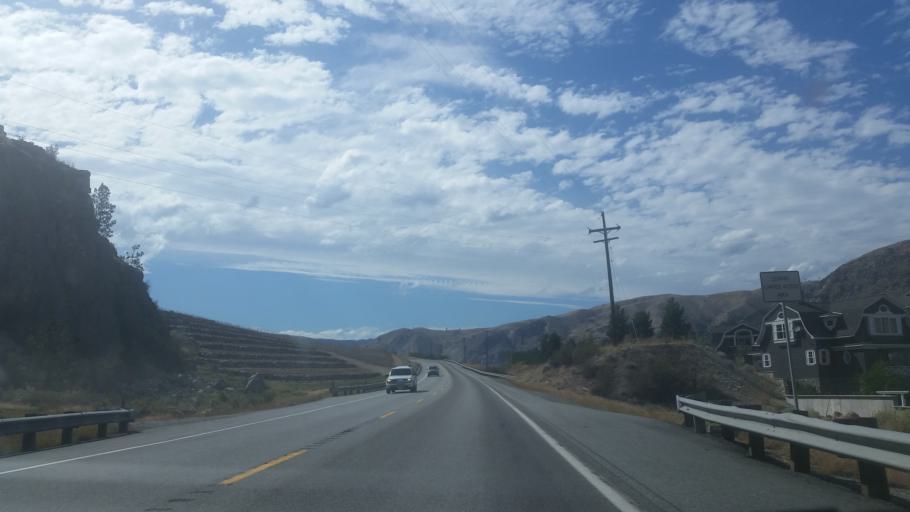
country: US
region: Washington
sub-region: Chelan County
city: Chelan
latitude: 47.7672
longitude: -120.1085
